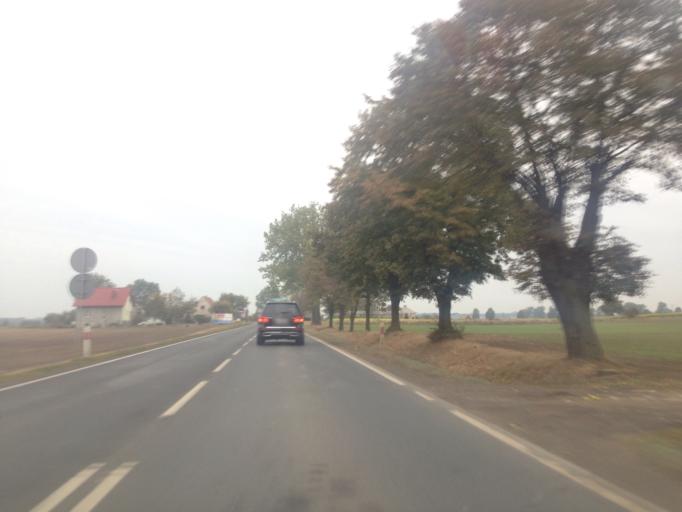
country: PL
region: Greater Poland Voivodeship
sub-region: Powiat gnieznienski
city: Niechanowo
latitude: 52.5531
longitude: 17.7116
